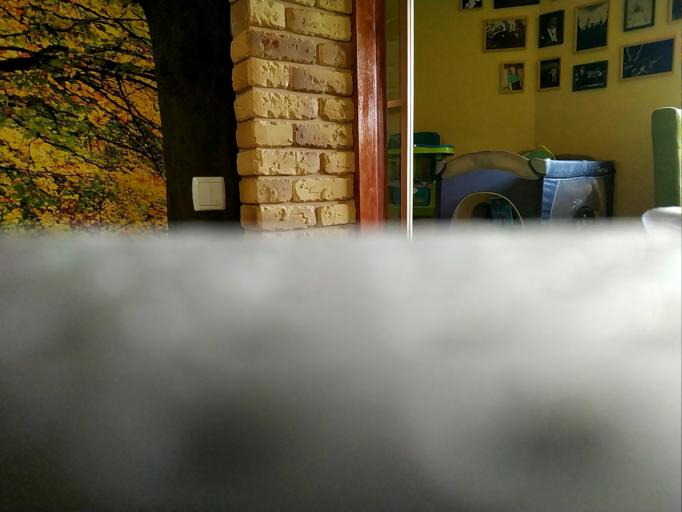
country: RU
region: Kaluga
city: Seredeyskiy
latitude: 53.9807
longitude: 35.3248
